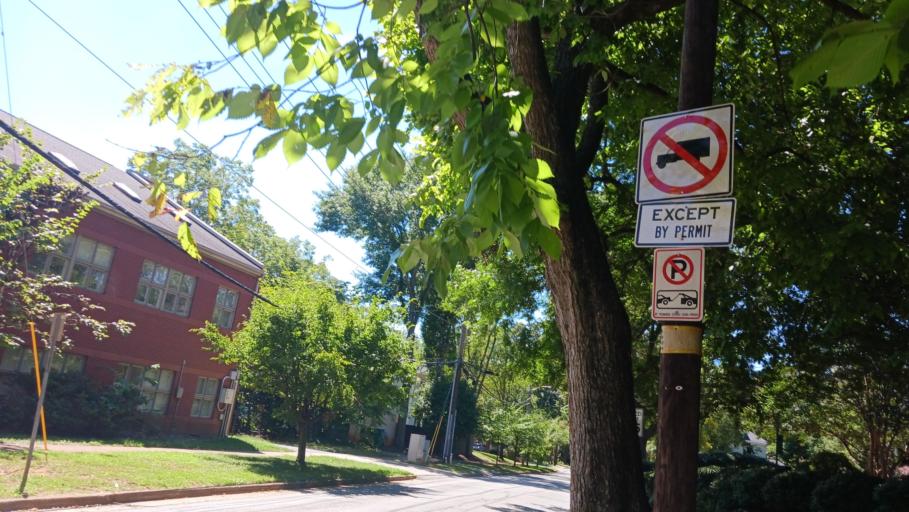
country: US
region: North Carolina
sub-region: Mecklenburg County
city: Charlotte
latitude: 35.2098
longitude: -80.8145
